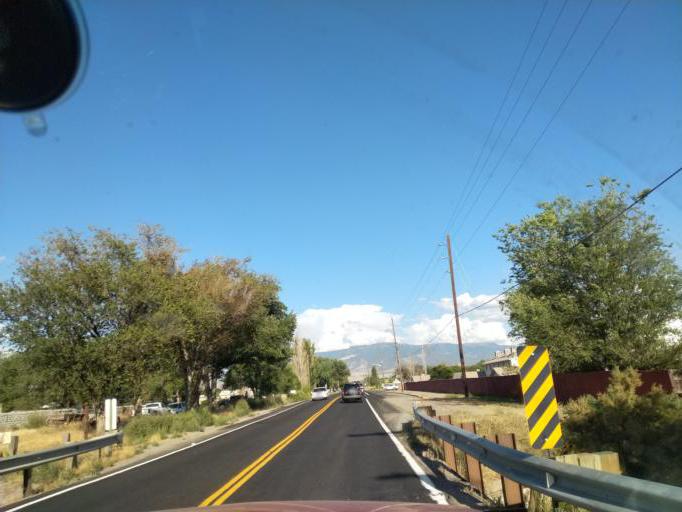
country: US
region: Colorado
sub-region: Mesa County
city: Fruitvale
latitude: 39.0628
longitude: -108.4780
